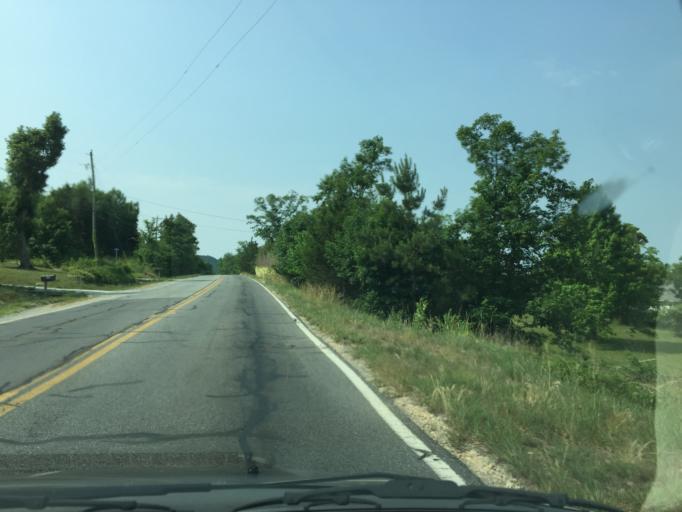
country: US
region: Georgia
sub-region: Catoosa County
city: Ringgold
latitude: 34.9251
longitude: -85.1041
